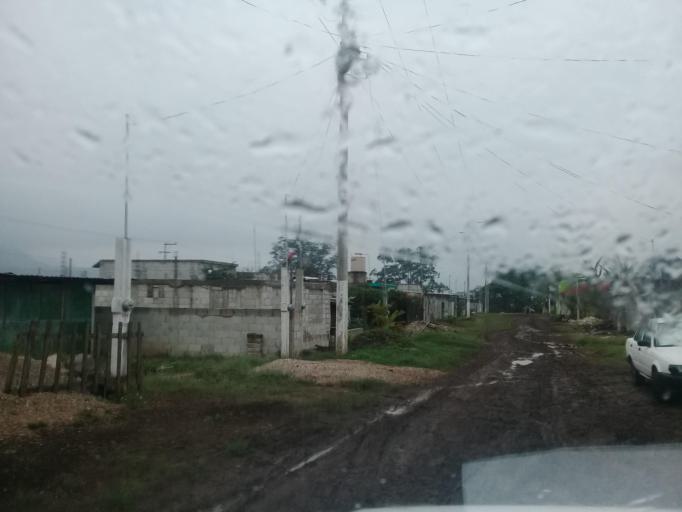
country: MX
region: Veracruz
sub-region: Cordoba
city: San Jose de Tapia
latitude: 18.8504
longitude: -96.9586
